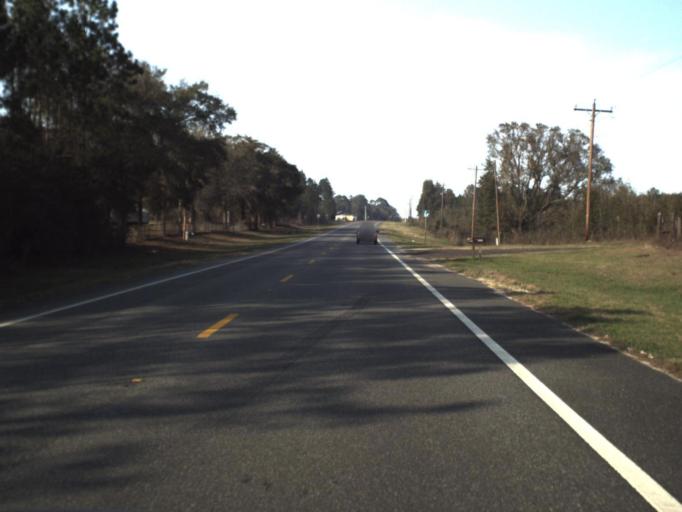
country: US
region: Florida
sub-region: Calhoun County
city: Blountstown
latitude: 30.5298
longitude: -85.1929
